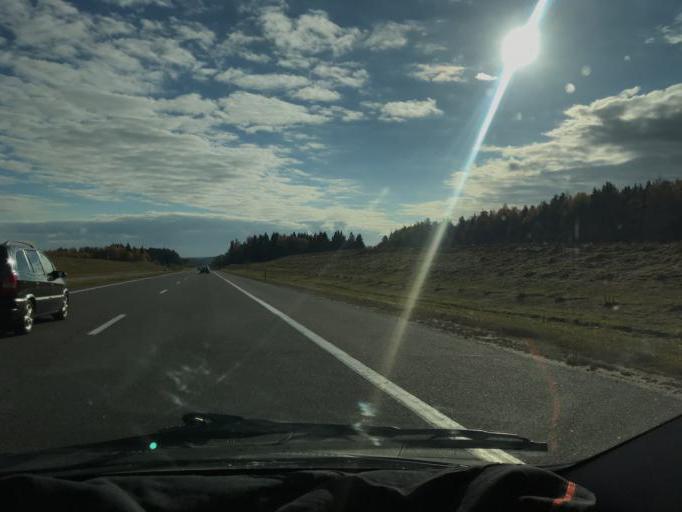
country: BY
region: Minsk
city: Lahoysk
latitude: 54.1446
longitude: 27.8095
